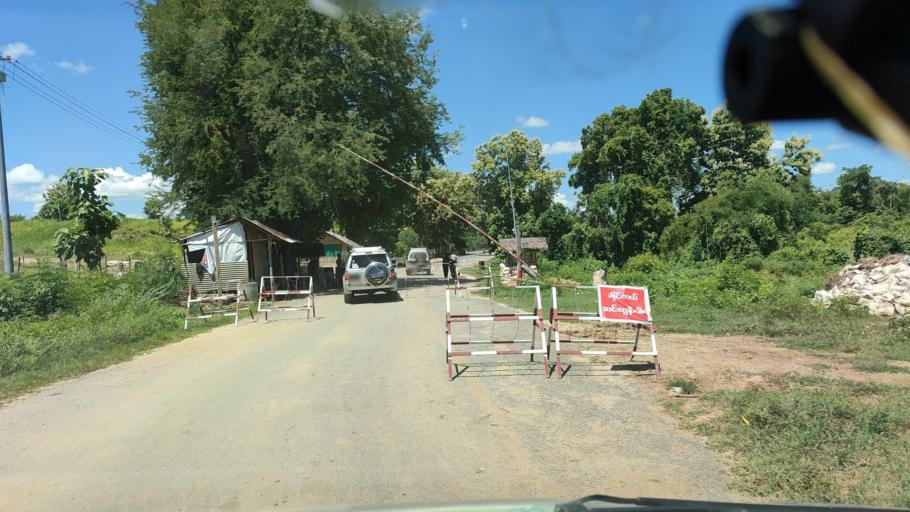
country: MM
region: Magway
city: Thayetmyo
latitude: 19.3411
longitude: 95.1613
